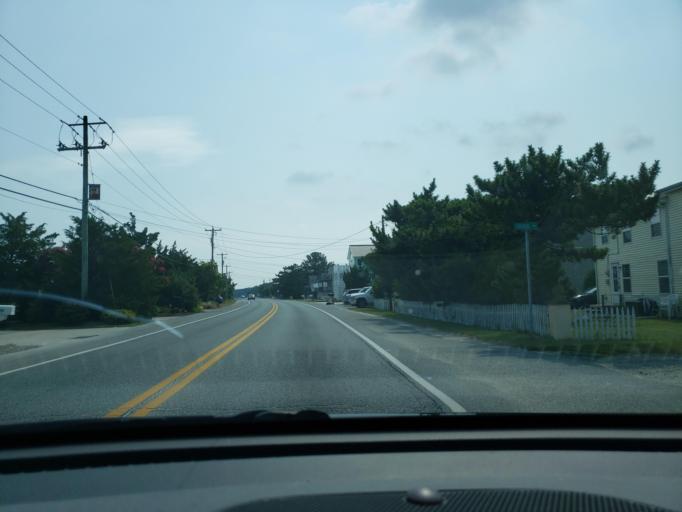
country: US
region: Delaware
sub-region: Sussex County
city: Lewes
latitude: 38.7805
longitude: -75.1319
